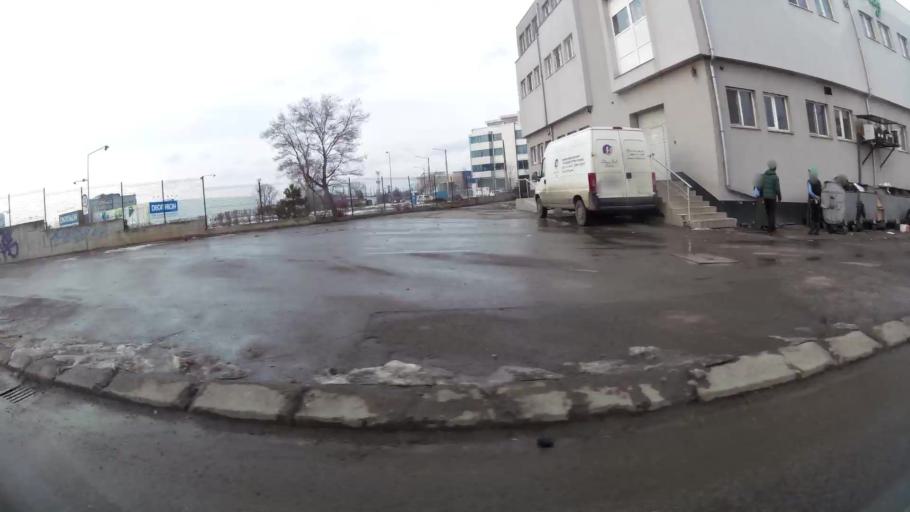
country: BG
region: Sofia-Capital
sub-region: Stolichna Obshtina
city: Sofia
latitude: 42.7092
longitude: 23.3717
